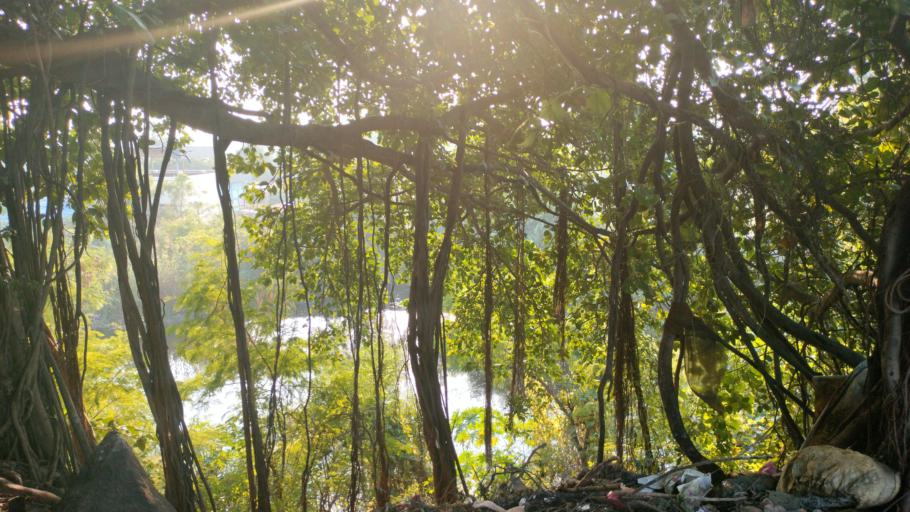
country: IN
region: Maharashtra
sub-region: Thane
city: Virar
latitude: 19.3959
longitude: 72.7818
